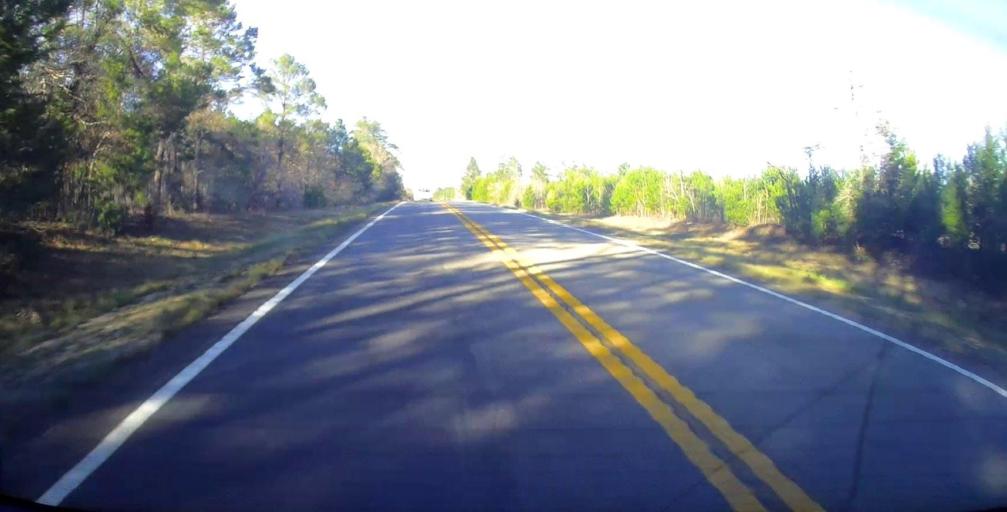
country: US
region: Georgia
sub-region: Taylor County
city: Butler
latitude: 32.5078
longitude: -84.3310
